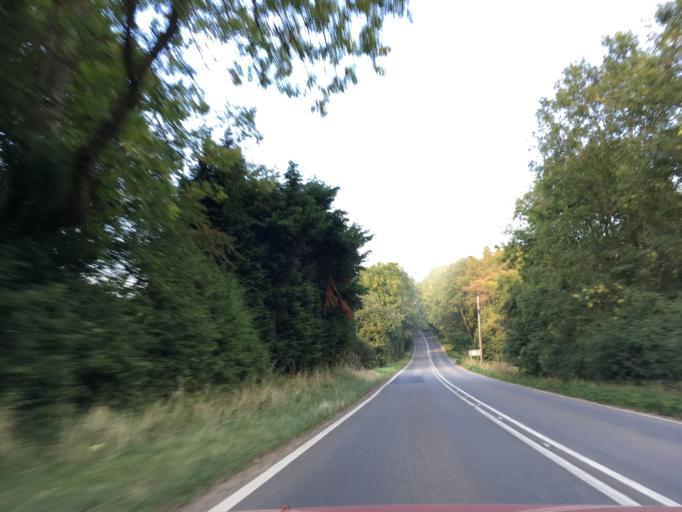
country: GB
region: England
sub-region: Gloucestershire
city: Bourton on the Water
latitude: 51.8667
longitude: -1.7957
